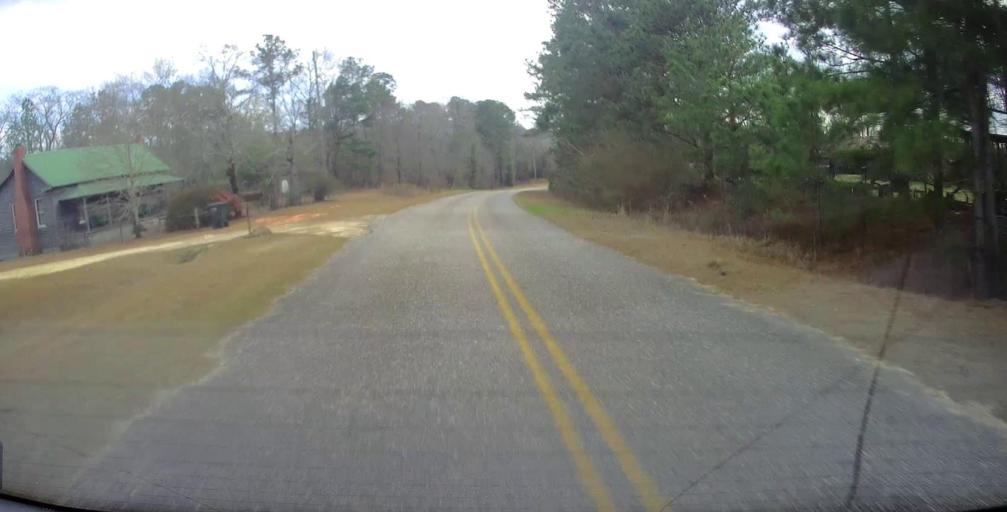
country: US
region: Georgia
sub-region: Marion County
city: Buena Vista
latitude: 32.4296
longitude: -84.4195
